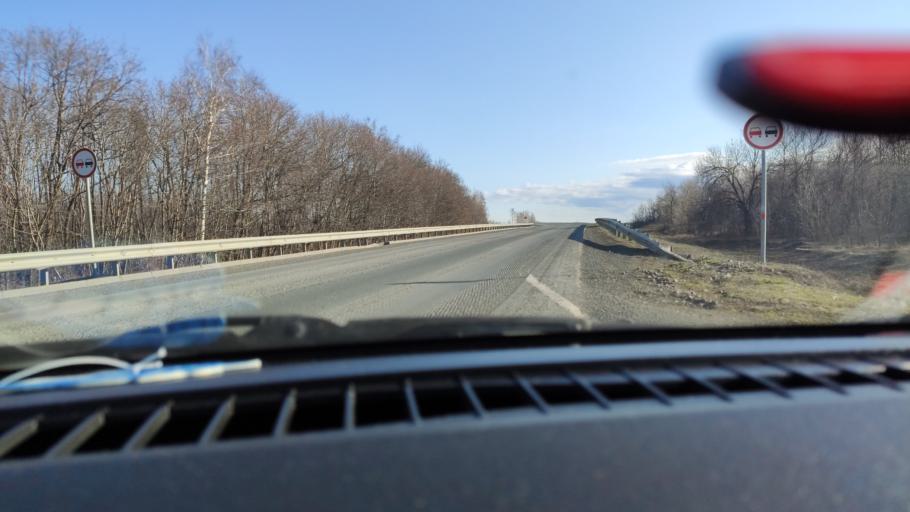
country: RU
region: Saratov
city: Dukhovnitskoye
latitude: 52.7096
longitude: 48.2643
